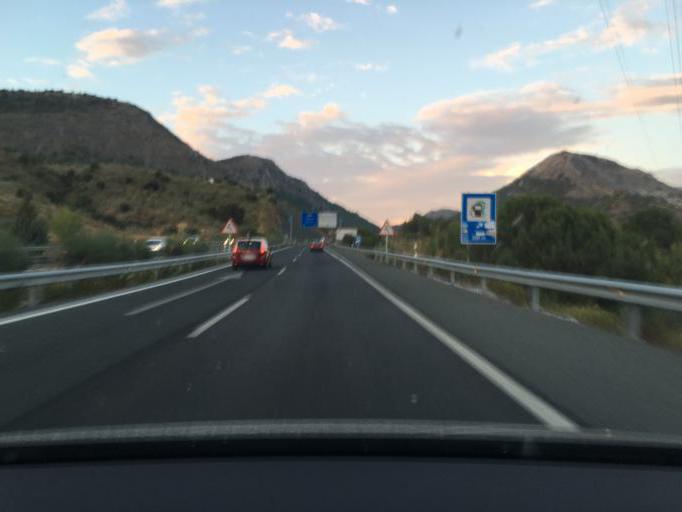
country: ES
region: Andalusia
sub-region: Provincia de Granada
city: Huetor Santillan
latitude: 37.2298
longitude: -3.5019
